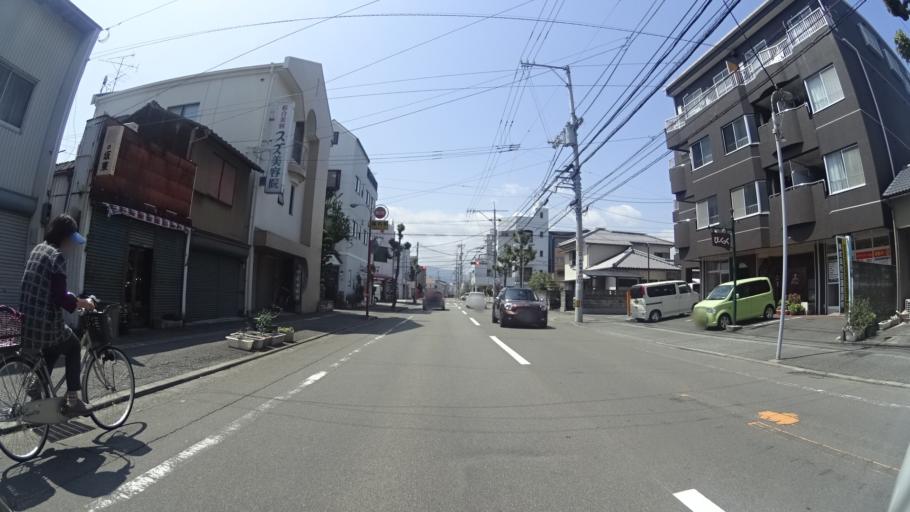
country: JP
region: Tokushima
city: Tokushima-shi
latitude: 34.0606
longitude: 134.5515
